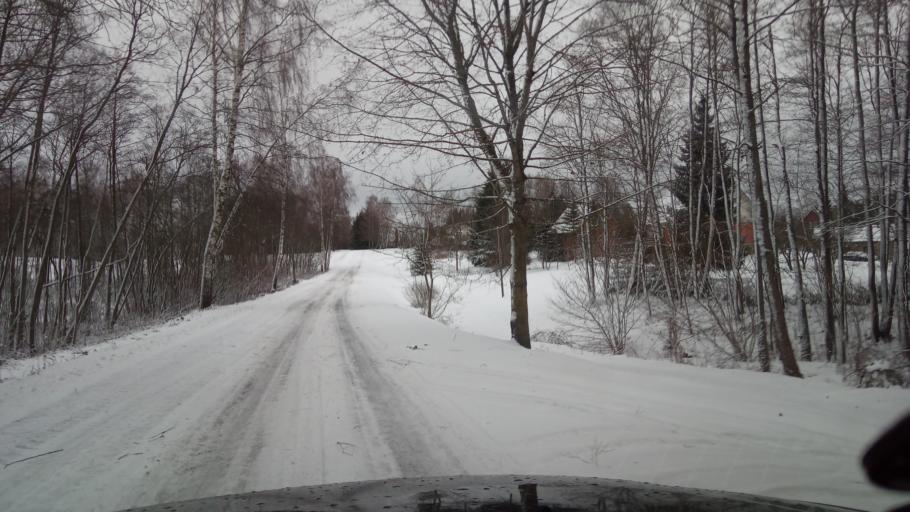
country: LT
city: Zarasai
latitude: 55.6227
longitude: 25.9545
